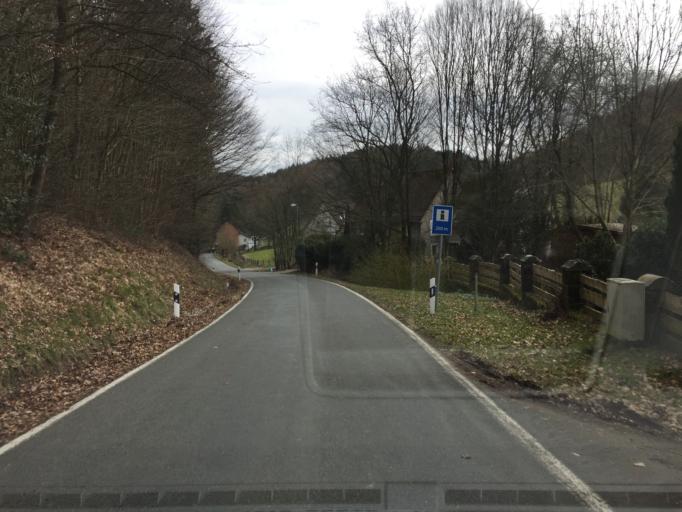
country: DE
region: North Rhine-Westphalia
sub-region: Regierungsbezirk Detmold
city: Detmold
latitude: 51.9006
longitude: 8.8516
